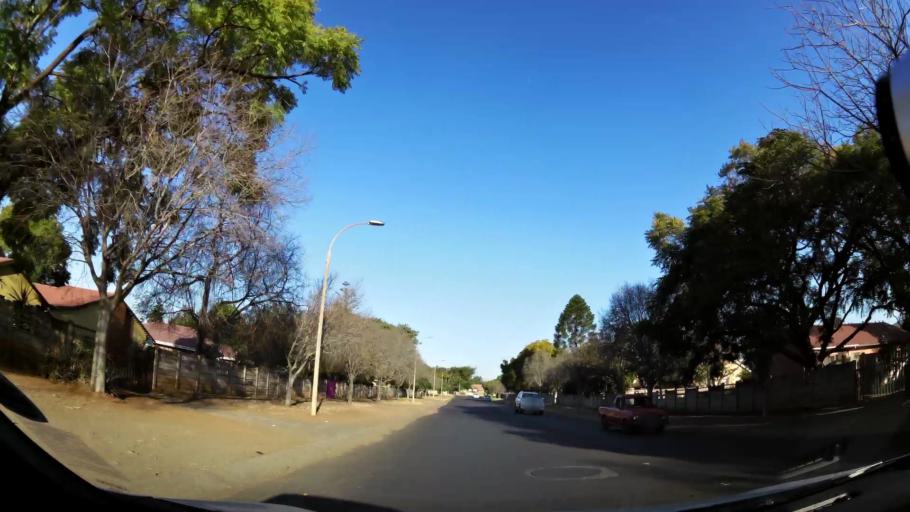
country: ZA
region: North-West
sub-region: Bojanala Platinum District Municipality
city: Rustenburg
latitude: -25.6815
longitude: 27.2173
